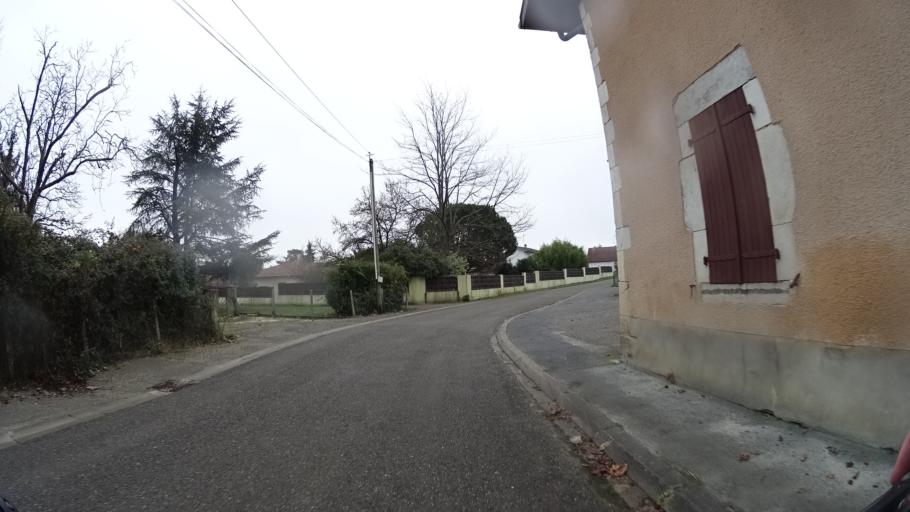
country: FR
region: Aquitaine
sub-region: Departement des Landes
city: Saint-Paul-les-Dax
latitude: 43.7319
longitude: -1.0504
